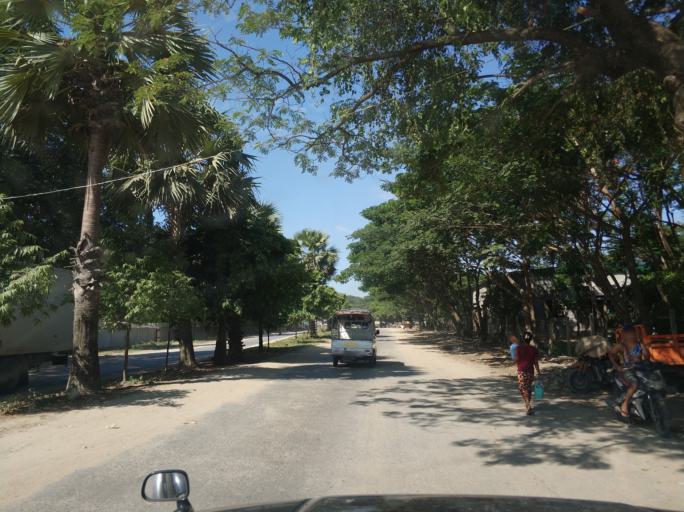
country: MM
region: Mandalay
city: Mandalay
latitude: 21.9599
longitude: 96.0537
